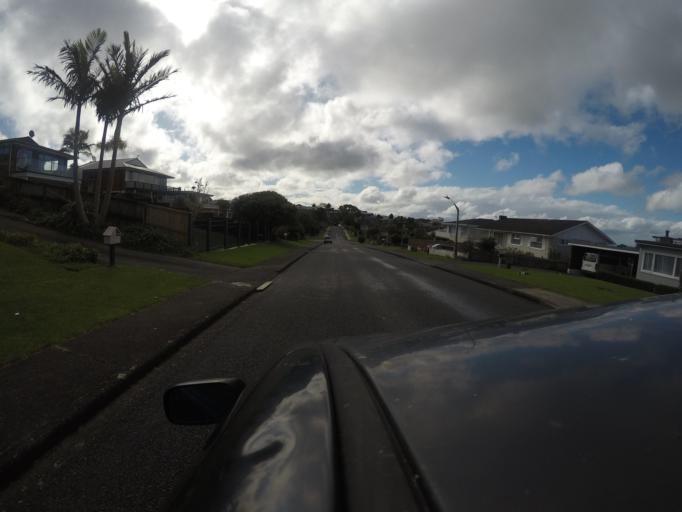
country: NZ
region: Auckland
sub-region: Auckland
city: Rosebank
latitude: -36.8904
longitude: 174.6460
